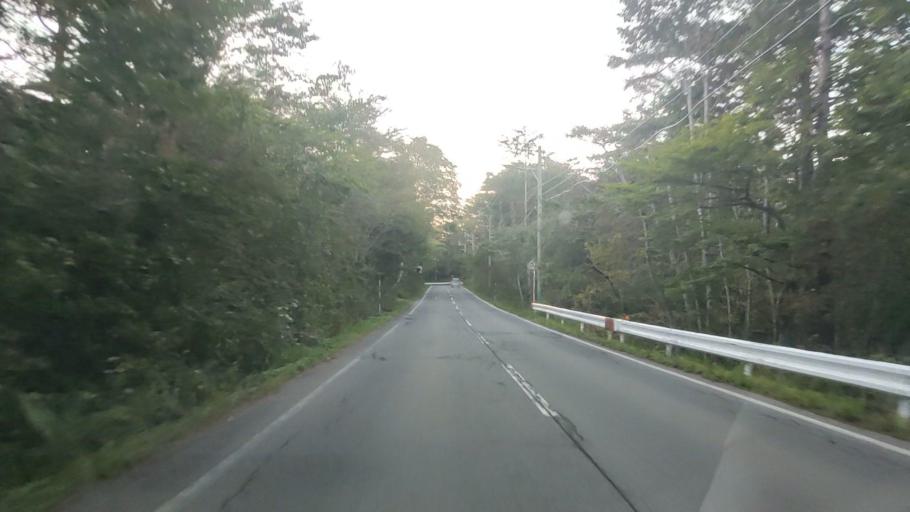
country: JP
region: Nagano
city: Komoro
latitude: 36.3987
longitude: 138.5811
